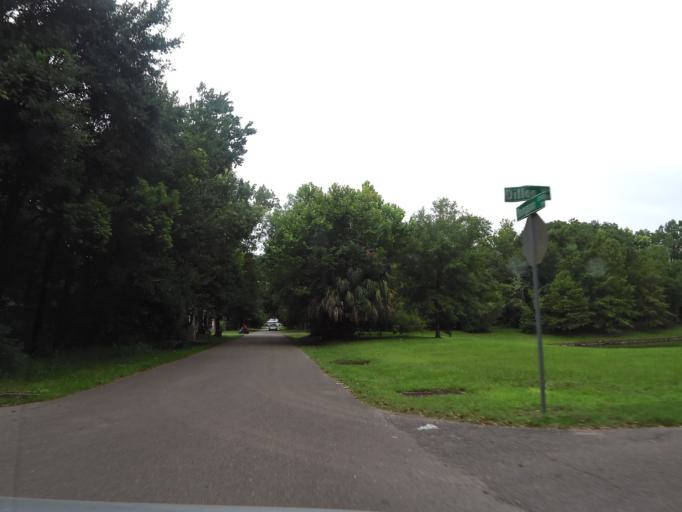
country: US
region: Florida
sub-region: Duval County
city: Jacksonville
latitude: 30.3254
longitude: -81.7156
